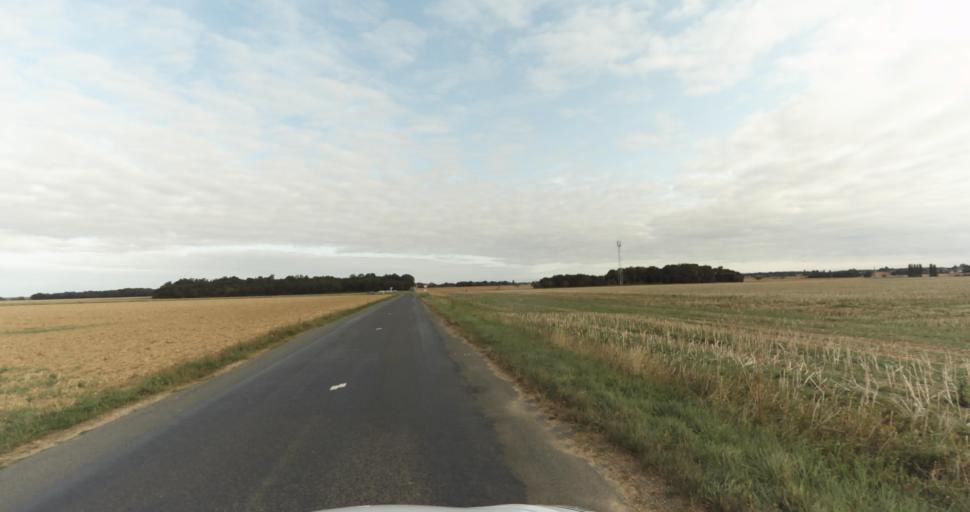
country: FR
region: Haute-Normandie
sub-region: Departement de l'Eure
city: Saint-Germain-sur-Avre
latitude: 48.8040
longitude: 1.2725
